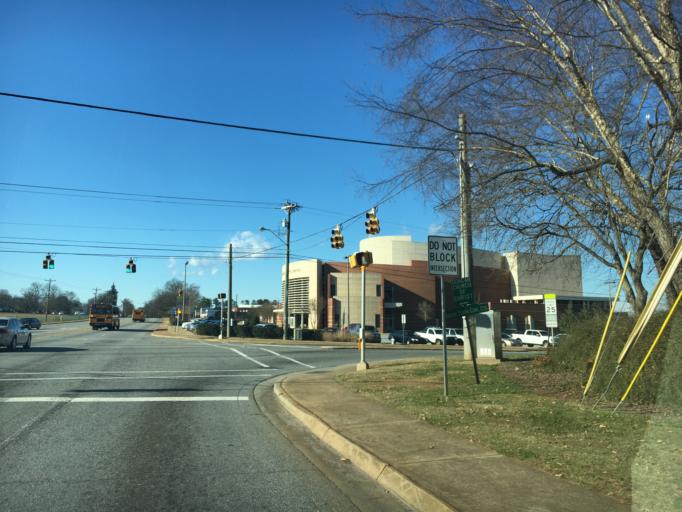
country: US
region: South Carolina
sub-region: Spartanburg County
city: Lyman
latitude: 34.9310
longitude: -82.1258
